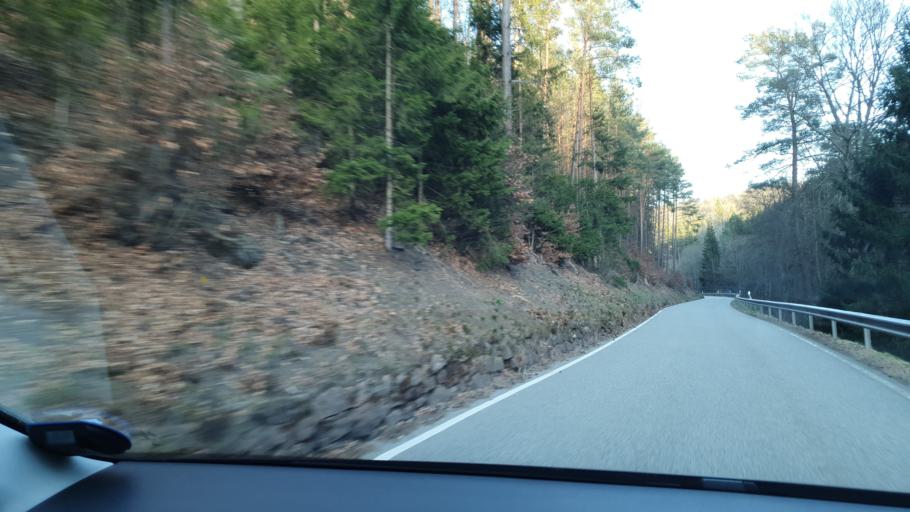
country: DE
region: Rheinland-Pfalz
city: Waldleiningen
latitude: 49.3965
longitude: 7.8595
